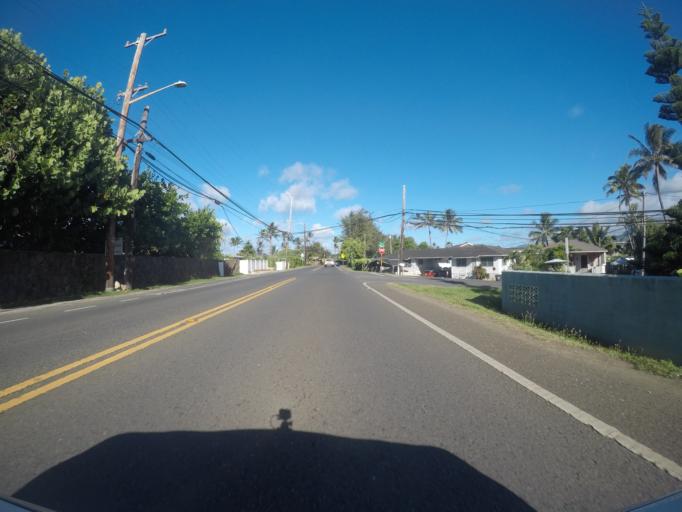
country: US
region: Hawaii
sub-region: Honolulu County
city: La'ie
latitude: 21.6508
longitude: -157.9258
